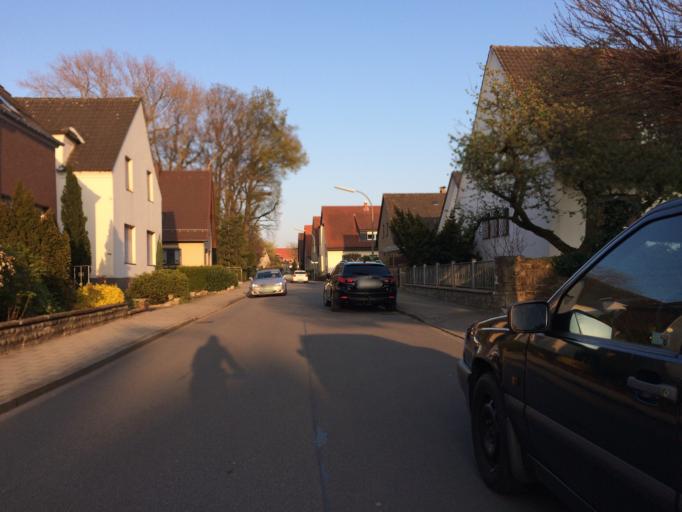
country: DE
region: Lower Saxony
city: Osnabrueck
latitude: 52.2522
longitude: 8.0947
